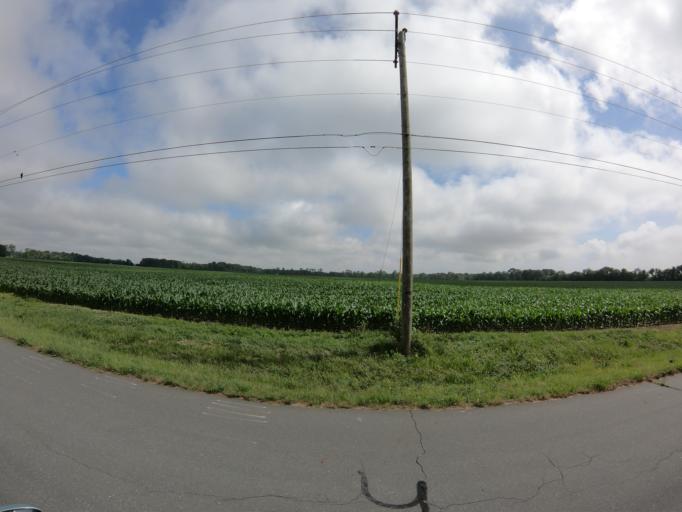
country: US
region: Delaware
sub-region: Kent County
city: Riverview
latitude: 39.0122
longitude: -75.4907
